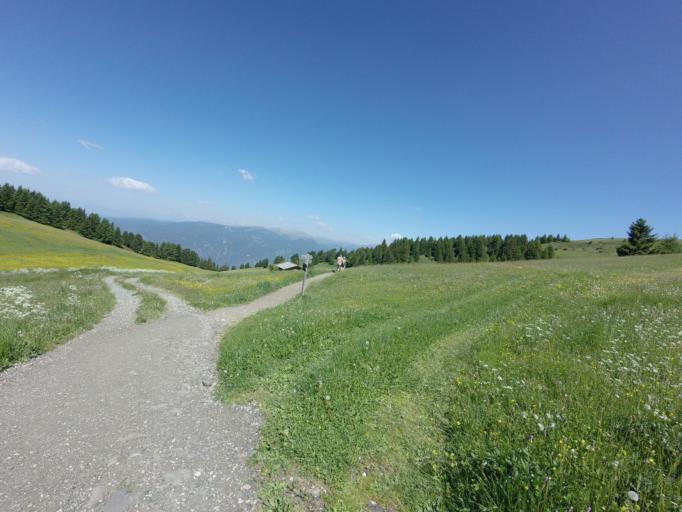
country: IT
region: Trentino-Alto Adige
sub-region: Bolzano
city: Castelrotto
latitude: 46.5524
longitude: 11.6011
